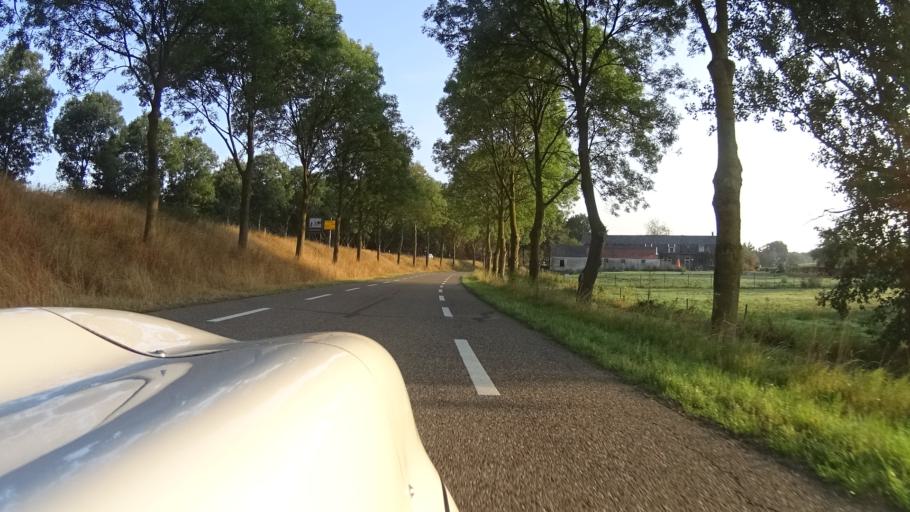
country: NL
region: Limburg
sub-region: Gemeente Bergen
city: Wellerlooi
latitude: 51.5526
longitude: 6.0982
